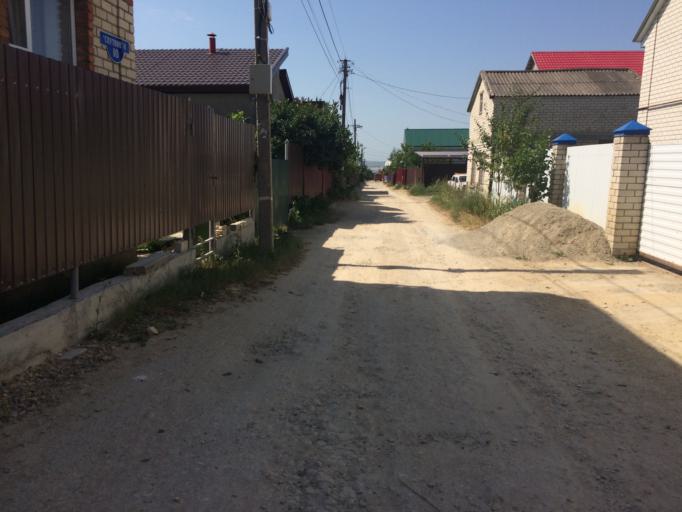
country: RU
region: Stavropol'skiy
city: Tatarka
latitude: 44.9866
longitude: 41.9422
